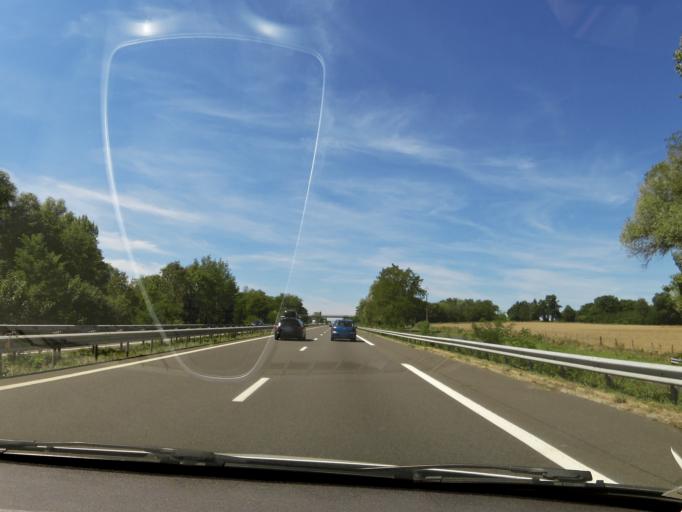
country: FR
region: Auvergne
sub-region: Departement du Puy-de-Dome
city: Orleat
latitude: 45.8497
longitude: 3.4300
